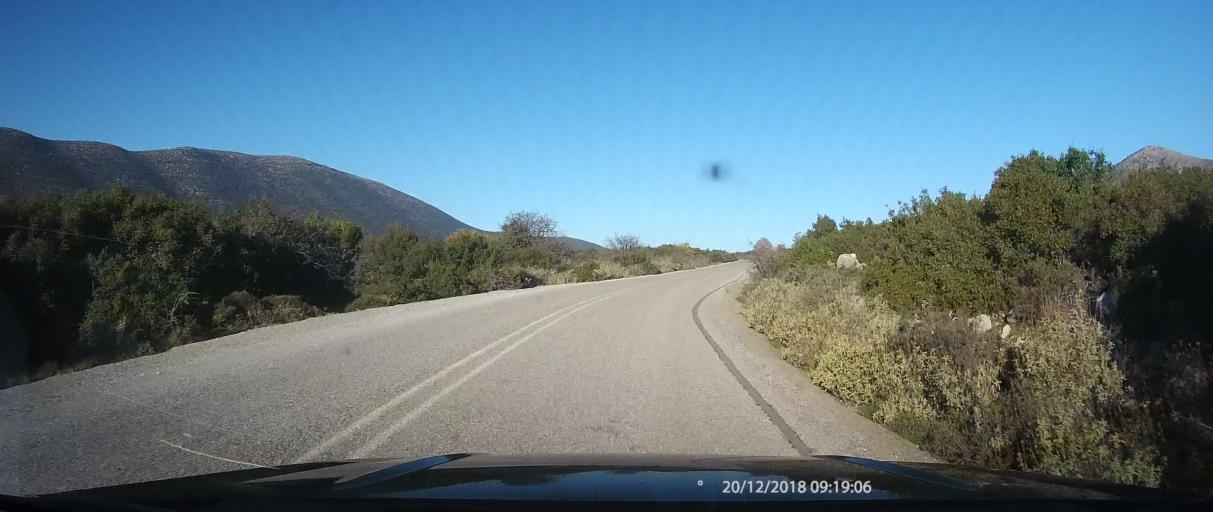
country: GR
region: Peloponnese
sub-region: Nomos Lakonias
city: Molaoi
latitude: 36.9157
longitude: 22.9450
